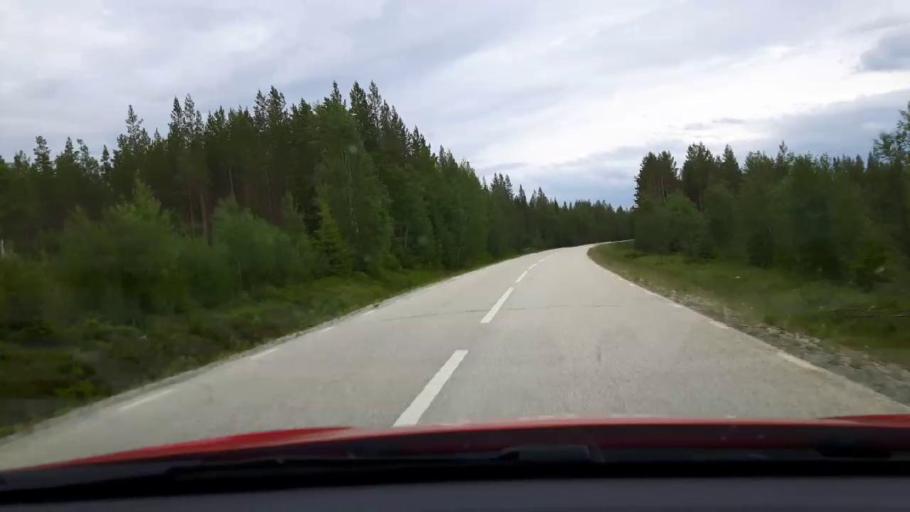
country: SE
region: Jaemtland
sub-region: Bergs Kommun
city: Hoverberg
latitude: 62.7172
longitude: 13.9212
